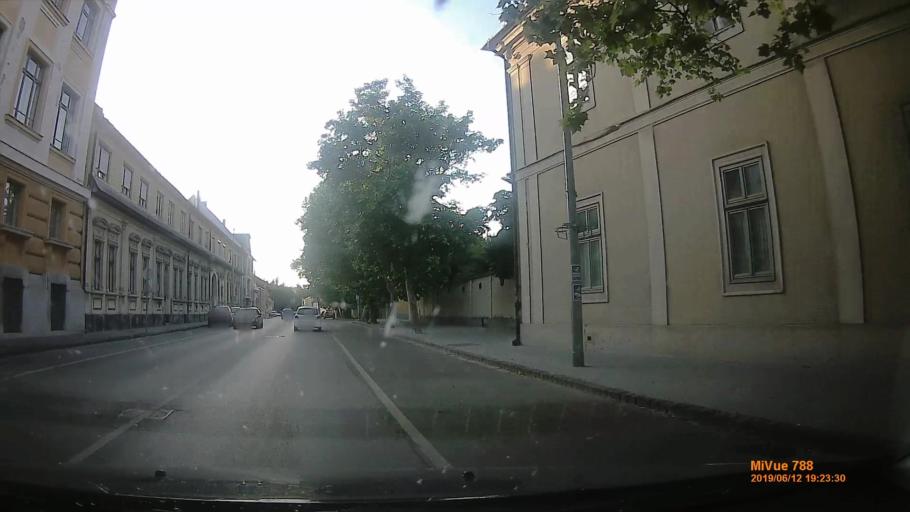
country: HU
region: Bacs-Kiskun
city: Kecskemet
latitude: 46.9108
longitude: 19.6916
